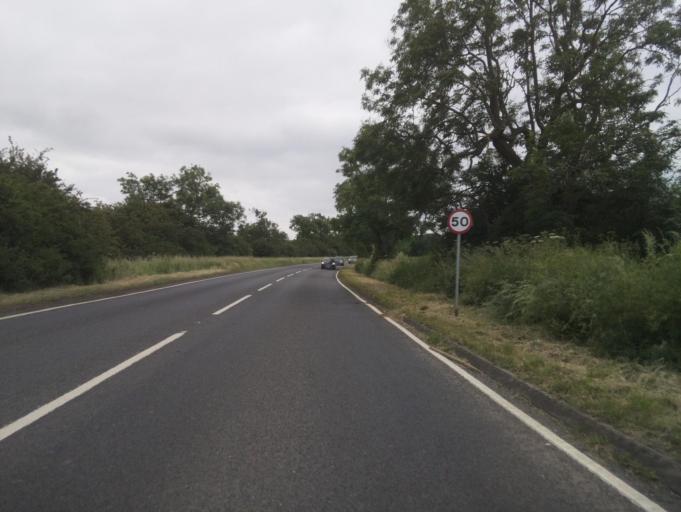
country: GB
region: England
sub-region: Leicestershire
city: Melton Mowbray
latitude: 52.7253
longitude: -0.8384
